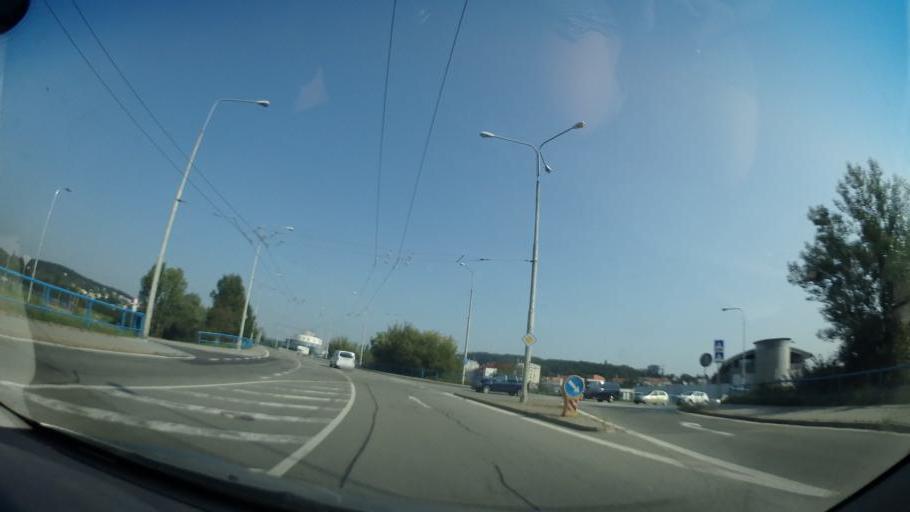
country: CZ
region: South Moravian
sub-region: Mesto Brno
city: Brno
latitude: 49.2114
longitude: 16.5592
